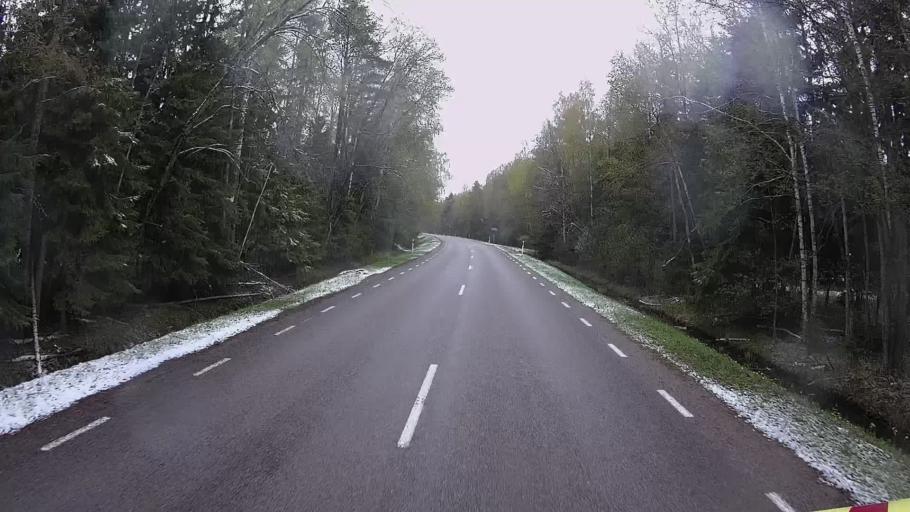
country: EE
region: Hiiumaa
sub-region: Kaerdla linn
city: Kardla
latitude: 58.8367
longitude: 22.4695
